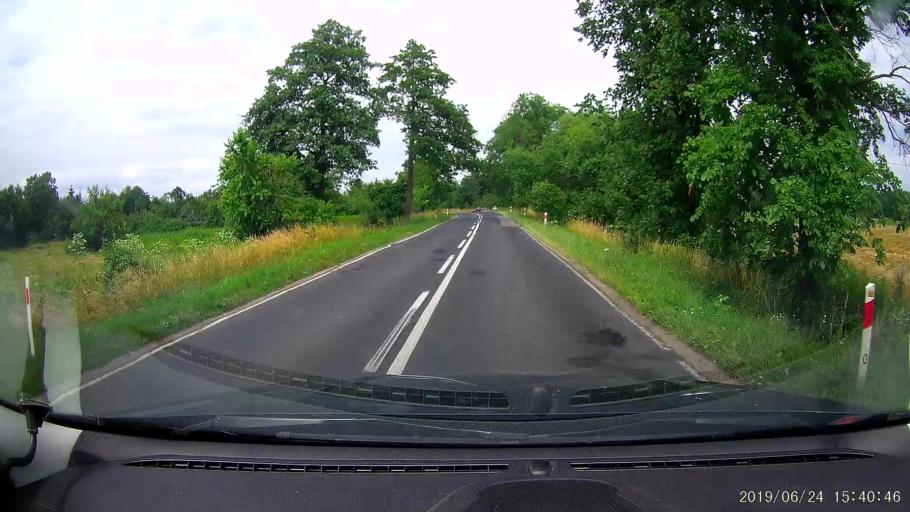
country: PL
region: Subcarpathian Voivodeship
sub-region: Powiat jaroslawski
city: Laszki
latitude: 50.1032
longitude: 22.8930
